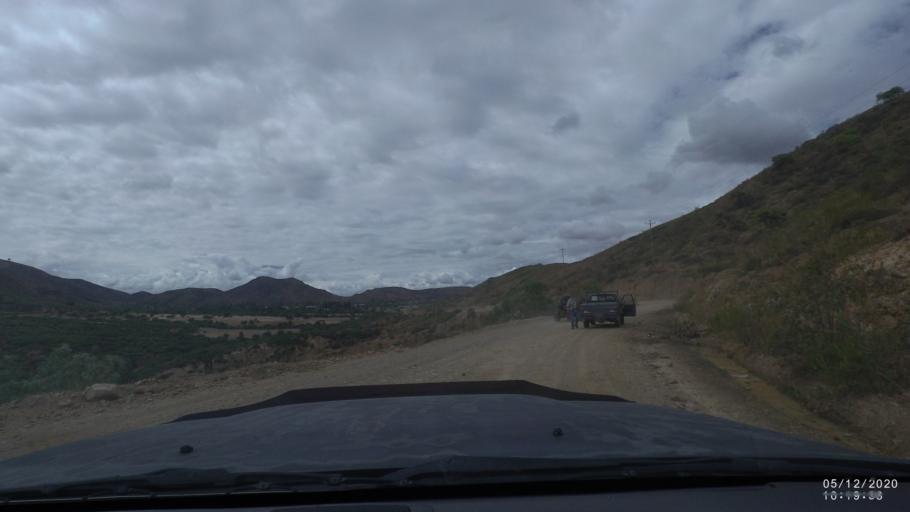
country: BO
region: Cochabamba
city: Sipe Sipe
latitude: -17.4809
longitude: -66.2829
